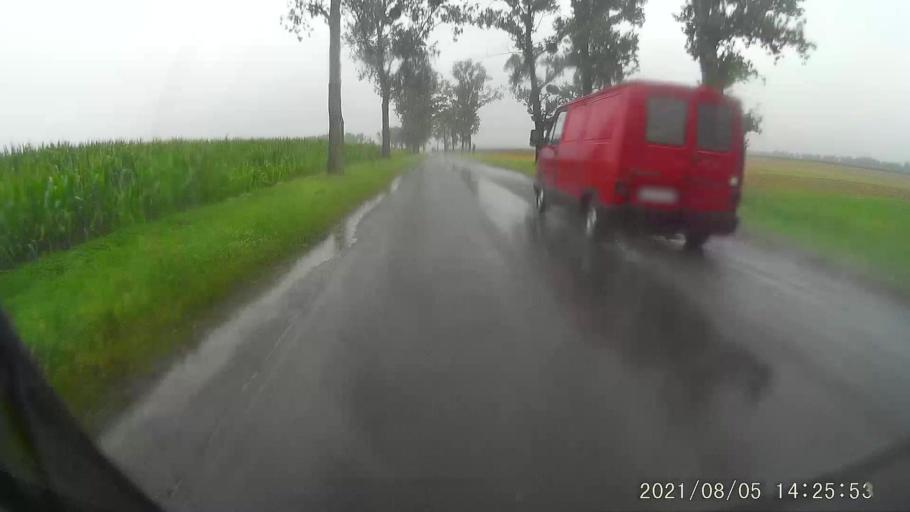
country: PL
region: Opole Voivodeship
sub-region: Powiat nyski
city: Korfantow
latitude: 50.4854
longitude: 17.6088
